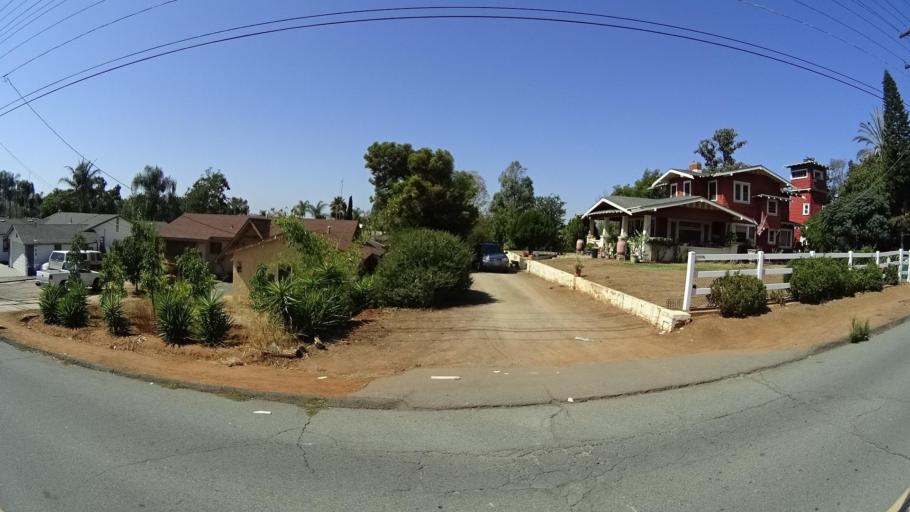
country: US
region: California
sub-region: San Diego County
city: Granite Hills
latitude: 32.8062
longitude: -116.9181
